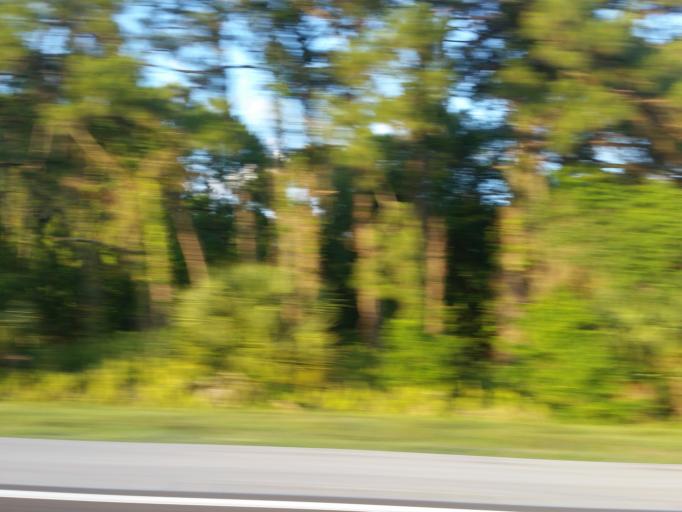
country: US
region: Florida
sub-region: Sarasota County
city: Nokomis
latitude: 27.1236
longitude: -82.3963
